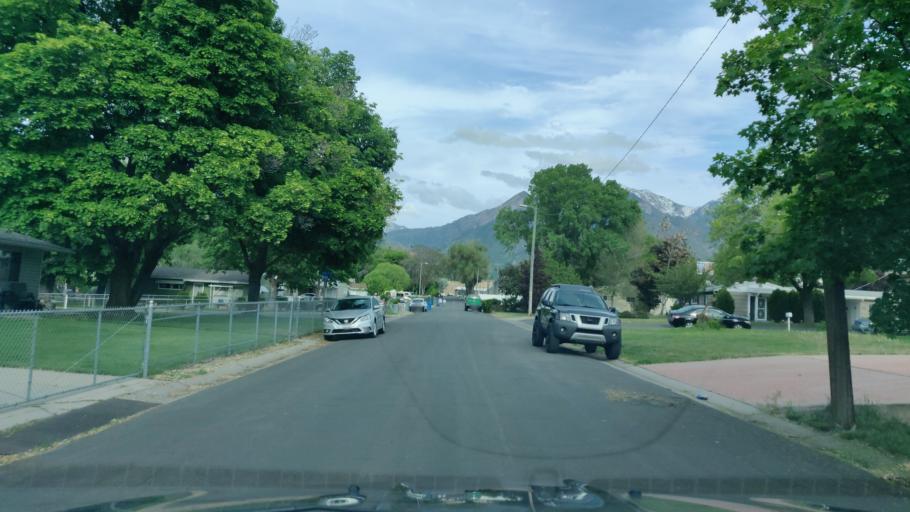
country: US
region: Utah
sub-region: Salt Lake County
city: Little Cottonwood Creek Valley
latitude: 40.6257
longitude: -111.8408
